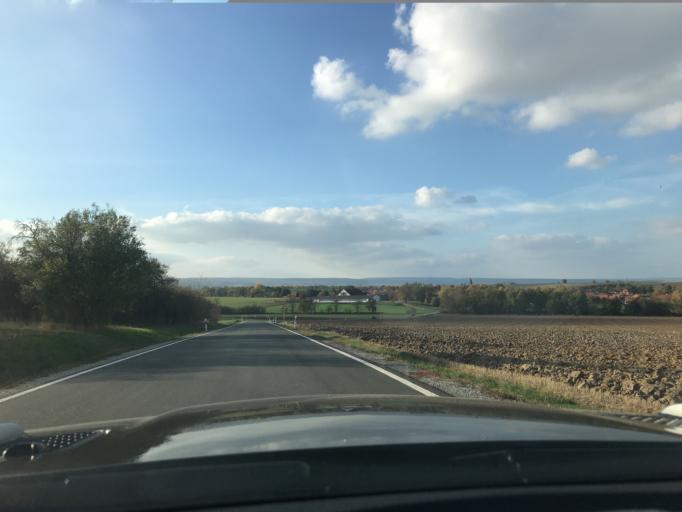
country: DE
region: Thuringia
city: Mulverstedt
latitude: 51.1211
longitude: 10.4886
